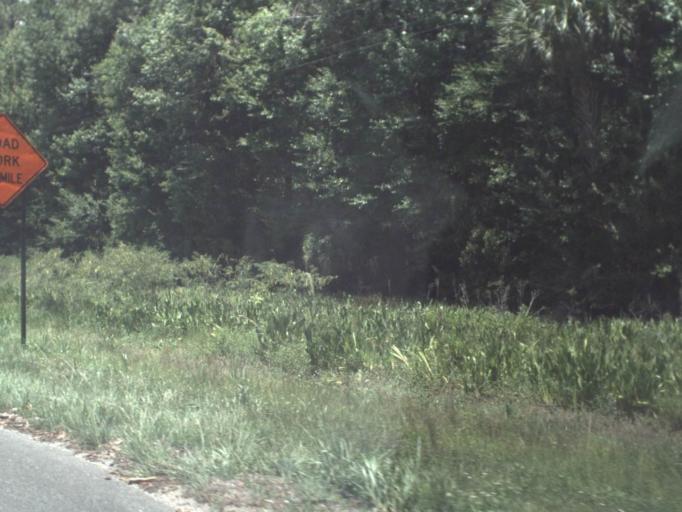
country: US
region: Florida
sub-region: Putnam County
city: Palatka
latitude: 29.5415
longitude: -81.7529
